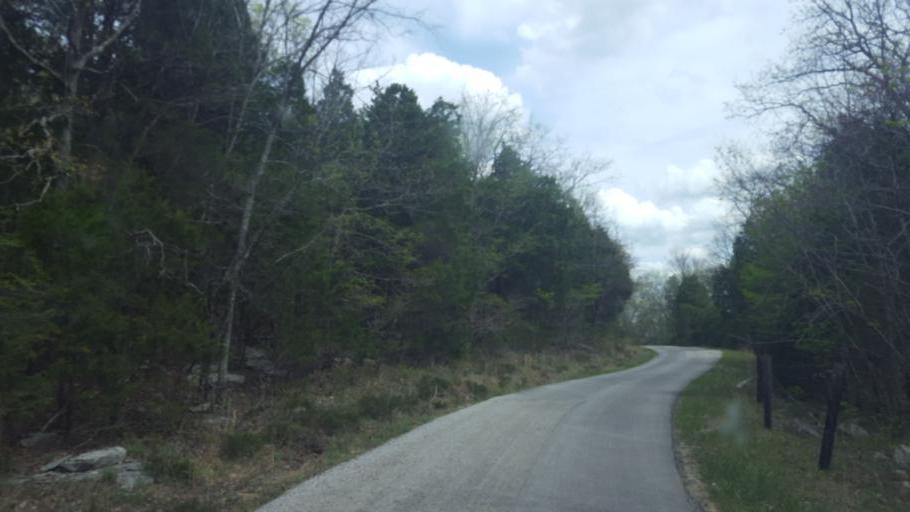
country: US
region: Kentucky
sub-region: Hart County
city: Munfordville
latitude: 37.2527
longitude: -85.9758
